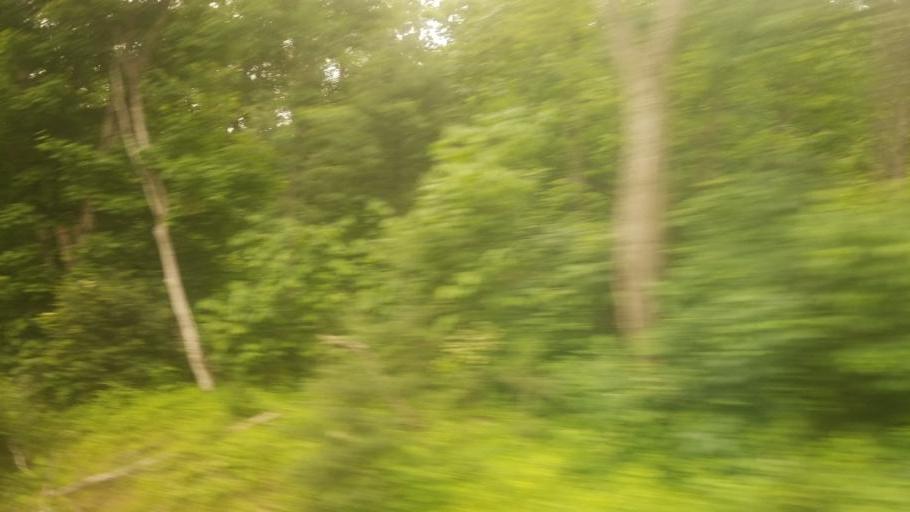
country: US
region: West Virginia
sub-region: Morgan County
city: Berkeley Springs
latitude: 39.6261
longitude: -78.3681
